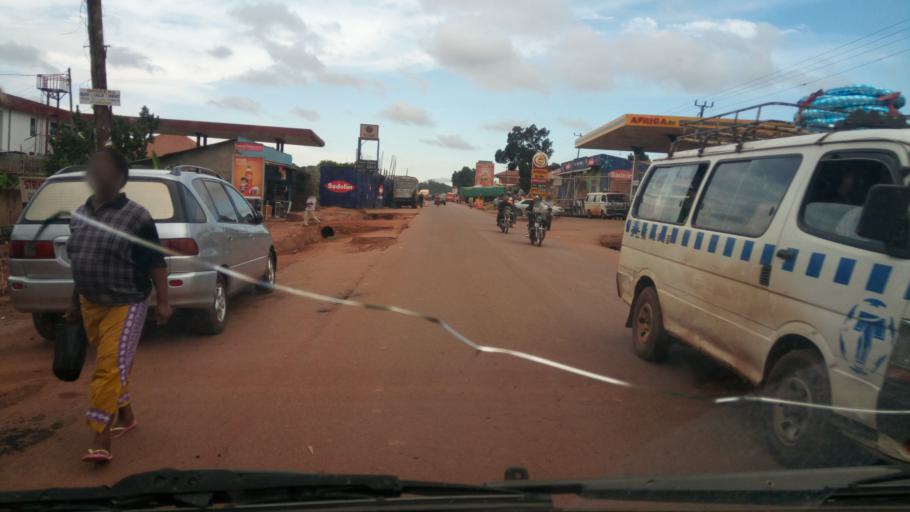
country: UG
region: Central Region
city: Kampala Central Division
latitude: 0.3328
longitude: 32.5525
